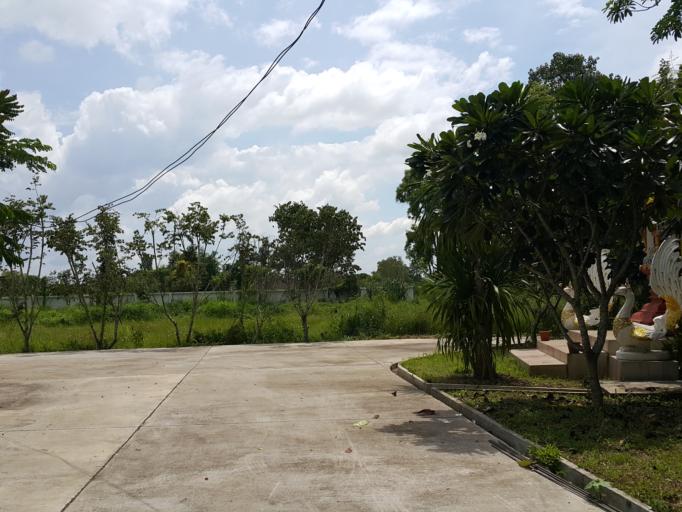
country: TH
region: Chiang Mai
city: San Kamphaeng
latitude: 18.7857
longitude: 99.1092
